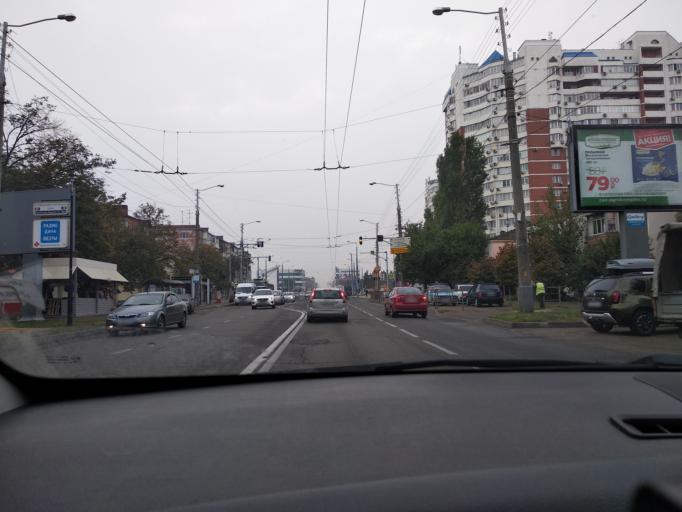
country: RU
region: Krasnodarskiy
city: Krasnodar
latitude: 45.0535
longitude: 38.9598
